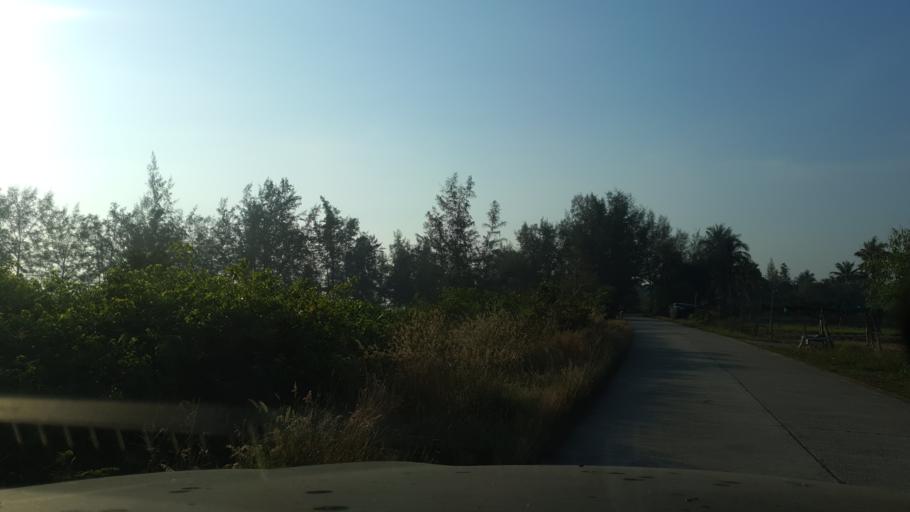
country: TH
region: Prachuap Khiri Khan
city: Bang Saphan
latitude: 11.2886
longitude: 99.5489
